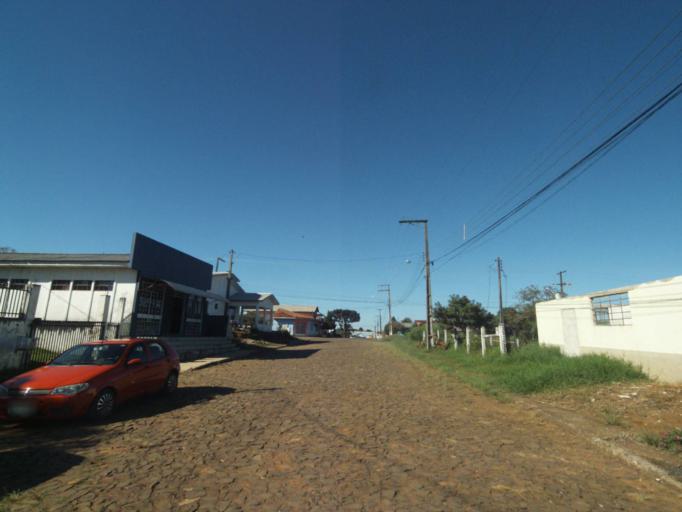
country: BR
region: Parana
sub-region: Pinhao
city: Pinhao
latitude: -25.8382
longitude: -52.0277
